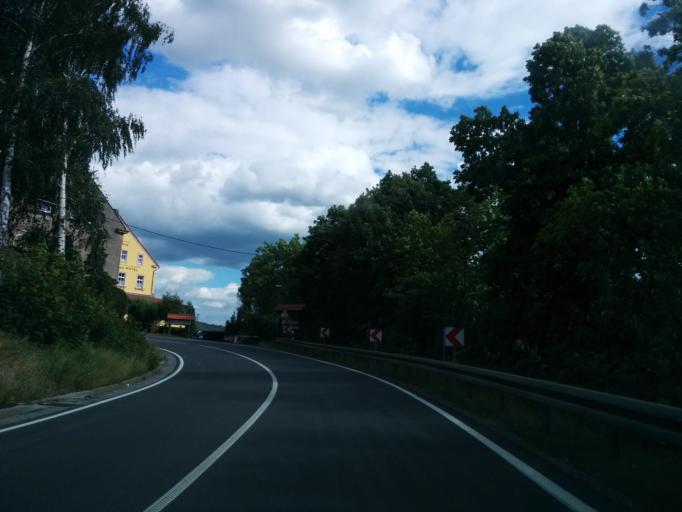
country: DE
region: Saxony
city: Falkenau
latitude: 50.8566
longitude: 13.1082
